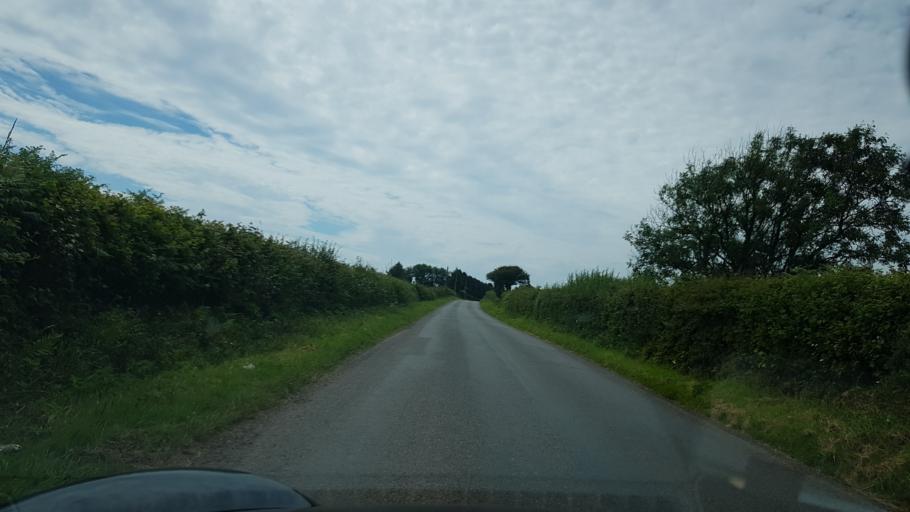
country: GB
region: Wales
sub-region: Carmarthenshire
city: Llanddowror
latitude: 51.7651
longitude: -4.5502
